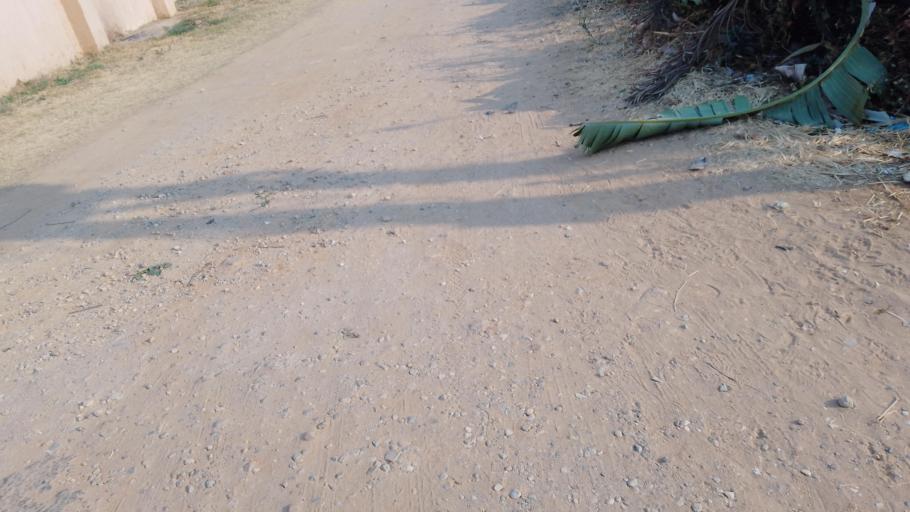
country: ZM
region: Lusaka
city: Lusaka
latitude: -15.3987
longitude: 28.3888
